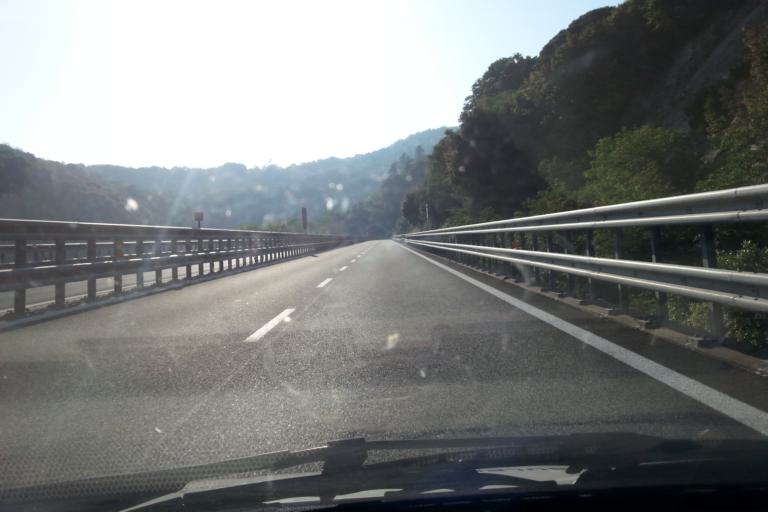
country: IT
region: Liguria
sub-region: Provincia di Savona
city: Vezzi Portio
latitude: 44.2271
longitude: 8.3744
